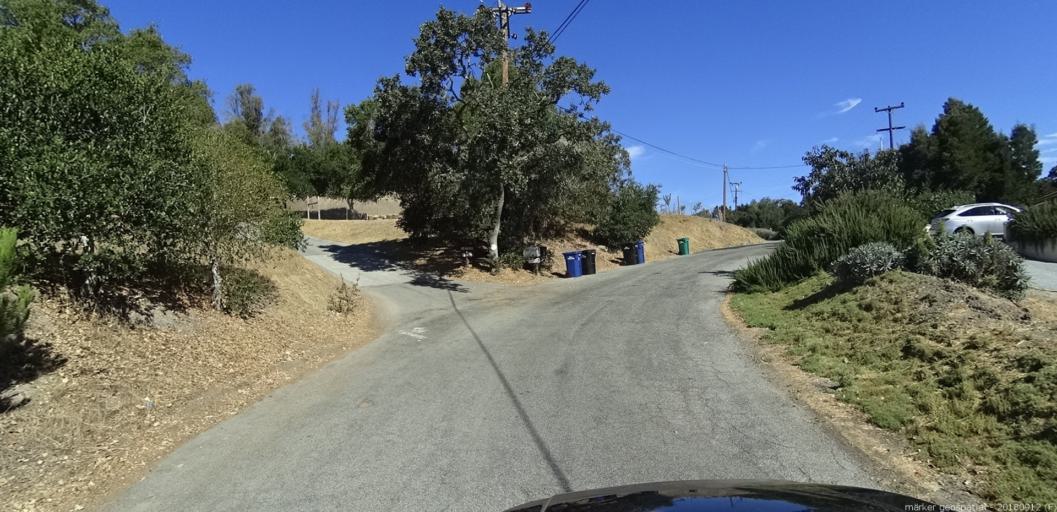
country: US
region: California
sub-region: Monterey County
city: Carmel Valley Village
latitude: 36.5677
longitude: -121.7315
